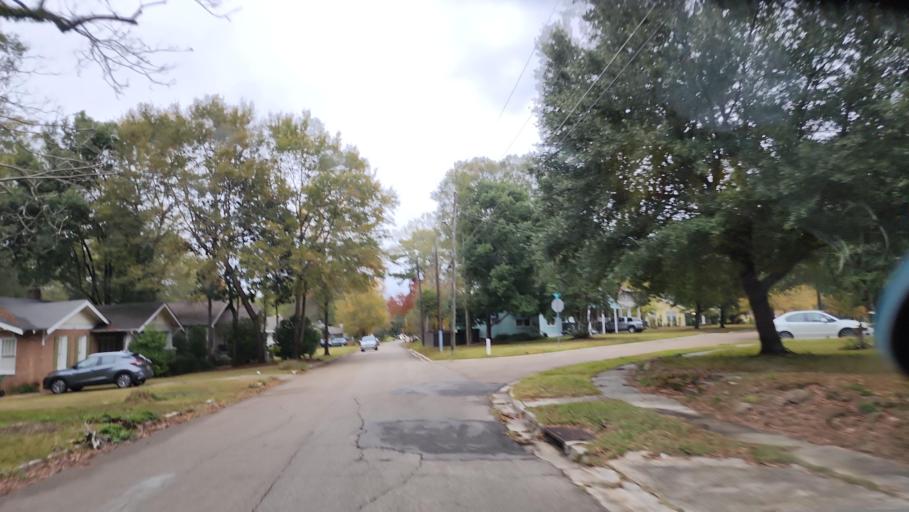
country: US
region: Mississippi
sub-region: Forrest County
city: Hattiesburg
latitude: 31.3213
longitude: -89.3058
